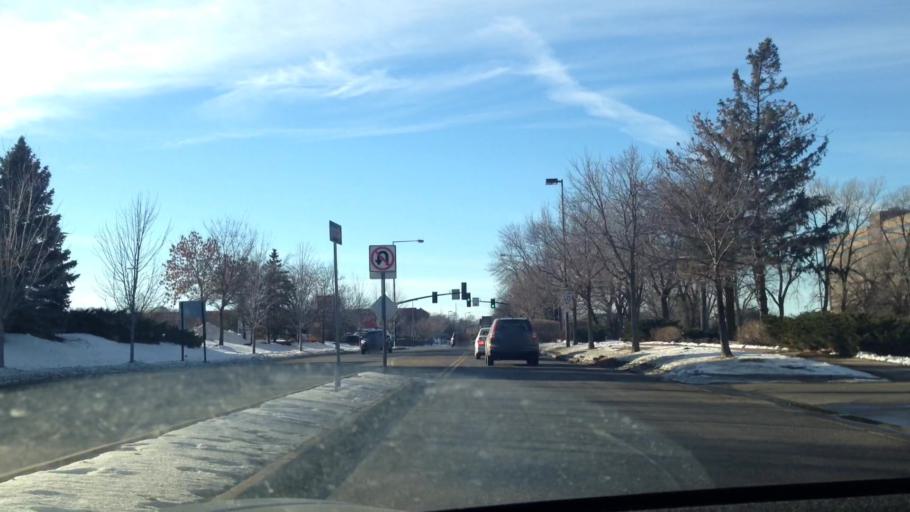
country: US
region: Minnesota
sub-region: Hennepin County
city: Saint Louis Park
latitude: 44.9677
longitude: -93.3500
